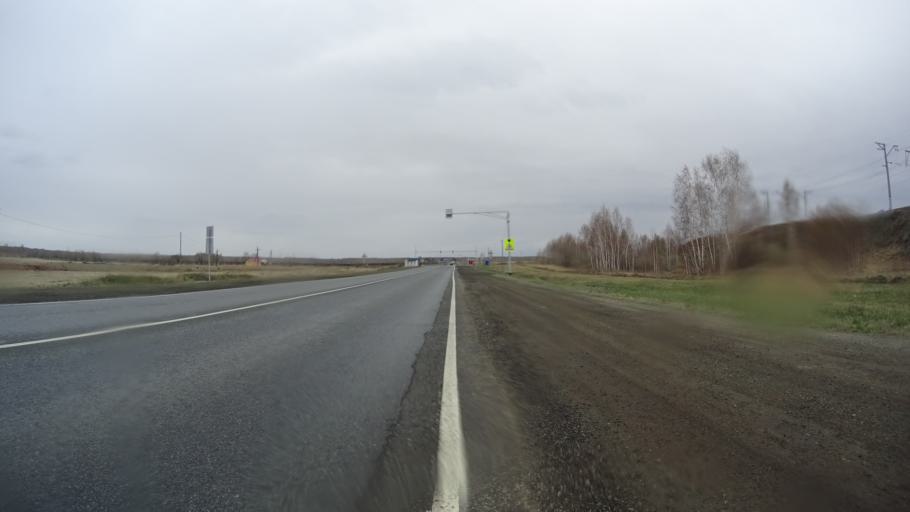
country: RU
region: Chelyabinsk
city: Krasnogorskiy
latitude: 54.6237
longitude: 61.2802
